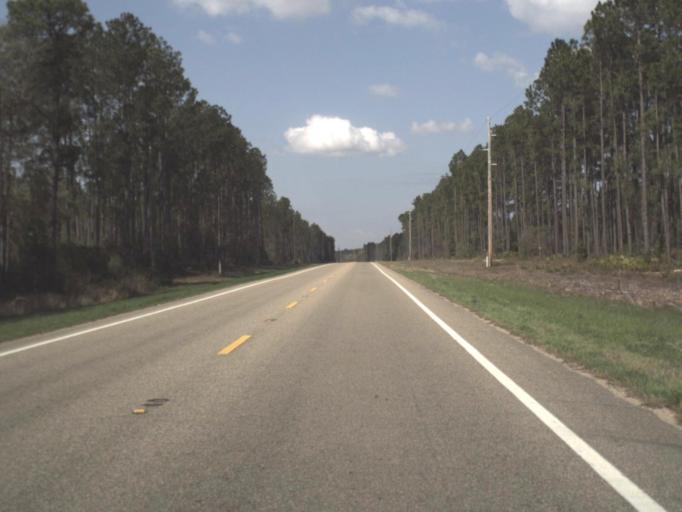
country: US
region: Florida
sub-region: Liberty County
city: Bristol
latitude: 30.4138
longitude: -84.8600
